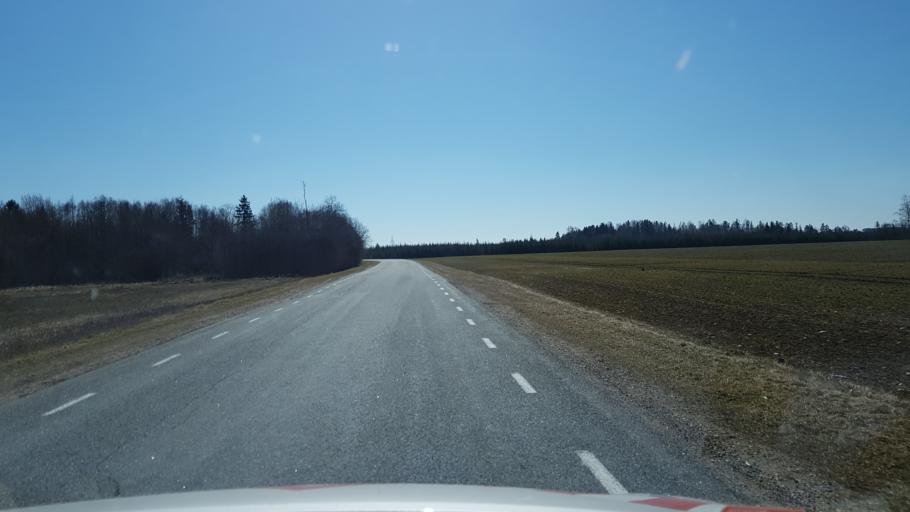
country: EE
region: Laeaene-Virumaa
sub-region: Rakke vald
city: Rakke
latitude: 59.0289
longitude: 26.3502
